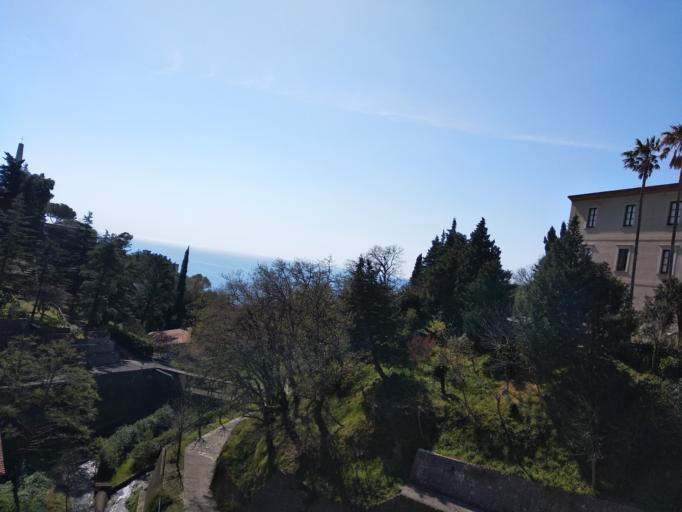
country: IT
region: Calabria
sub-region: Provincia di Cosenza
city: Paola
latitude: 39.3689
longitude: 16.0452
